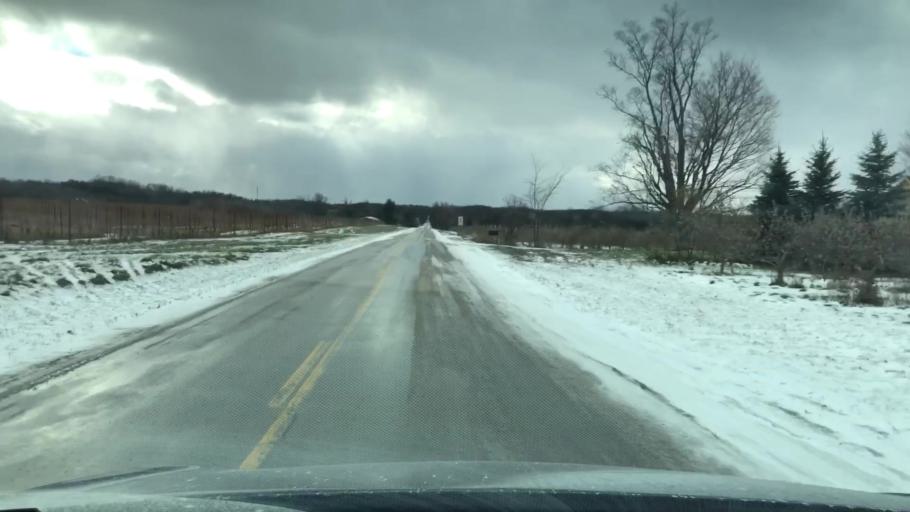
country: US
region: Michigan
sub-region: Antrim County
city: Elk Rapids
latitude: 44.9206
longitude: -85.5156
